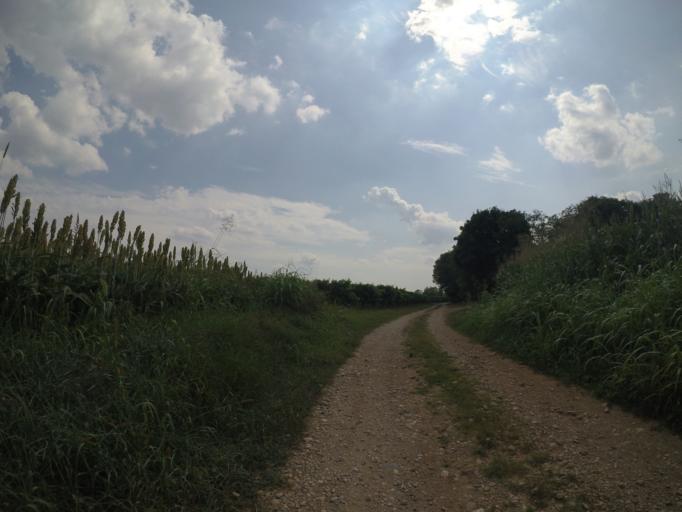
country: IT
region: Friuli Venezia Giulia
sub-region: Provincia di Udine
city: Bertiolo
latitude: 45.9536
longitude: 13.0718
